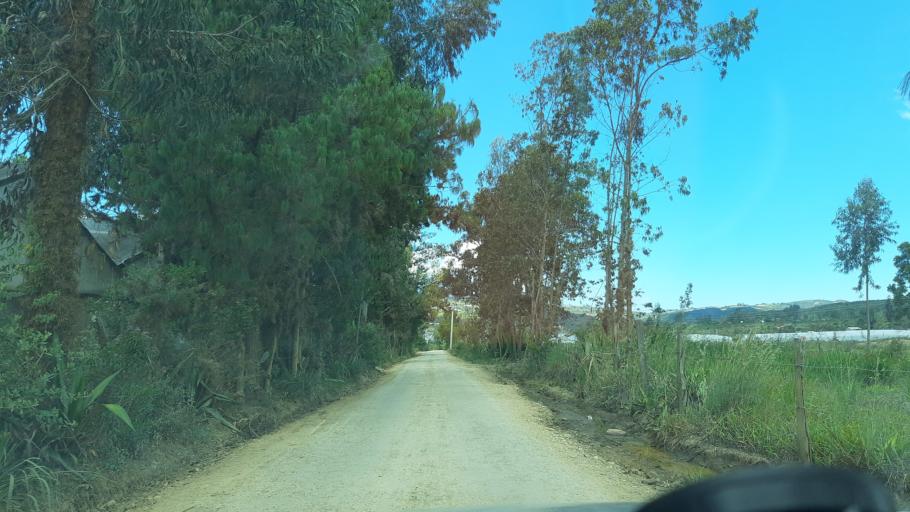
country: CO
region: Boyaca
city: Villa de Leiva
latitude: 5.6644
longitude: -73.5731
